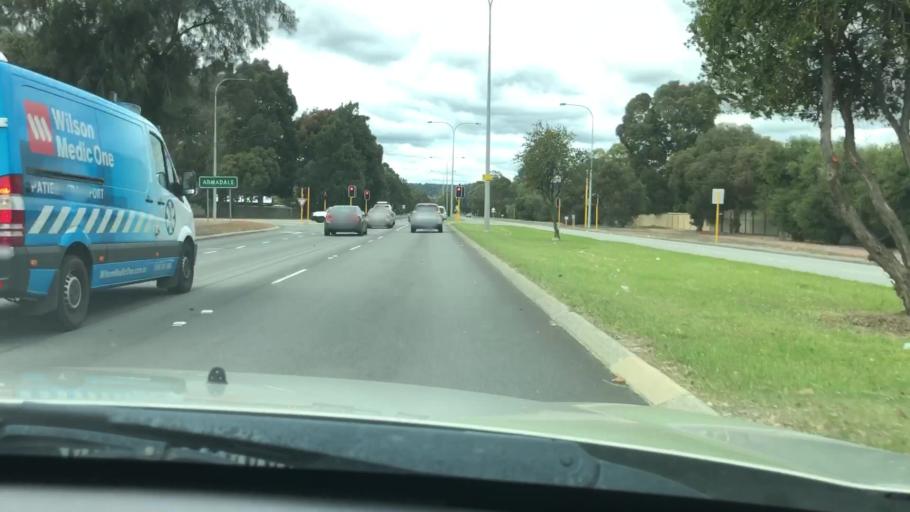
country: AU
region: Western Australia
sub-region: Armadale
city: Seville Grove
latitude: -32.1470
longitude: 115.9900
